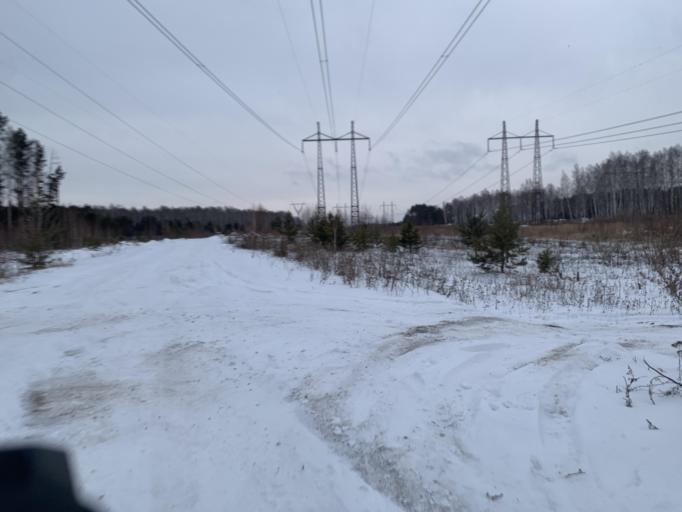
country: RU
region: Chelyabinsk
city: Roshchino
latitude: 55.1994
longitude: 61.2618
